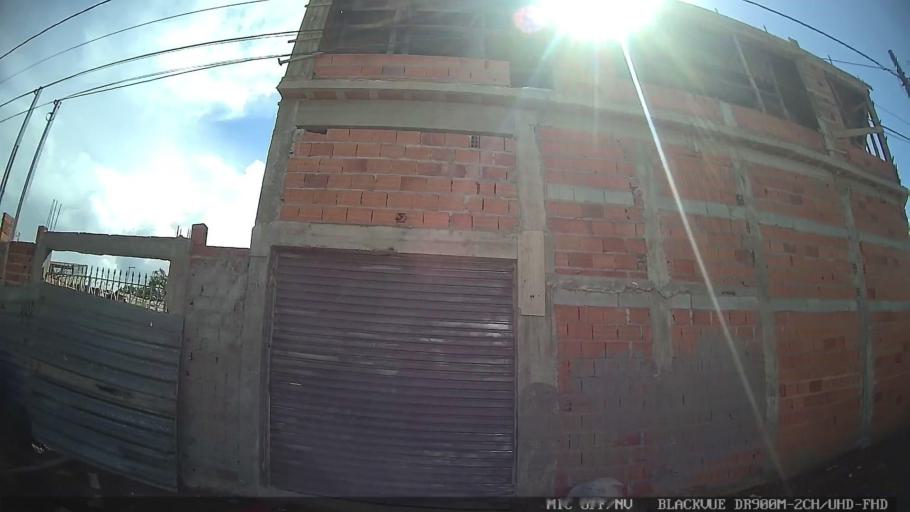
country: BR
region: Sao Paulo
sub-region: Itanhaem
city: Itanhaem
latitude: -24.2402
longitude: -46.8954
